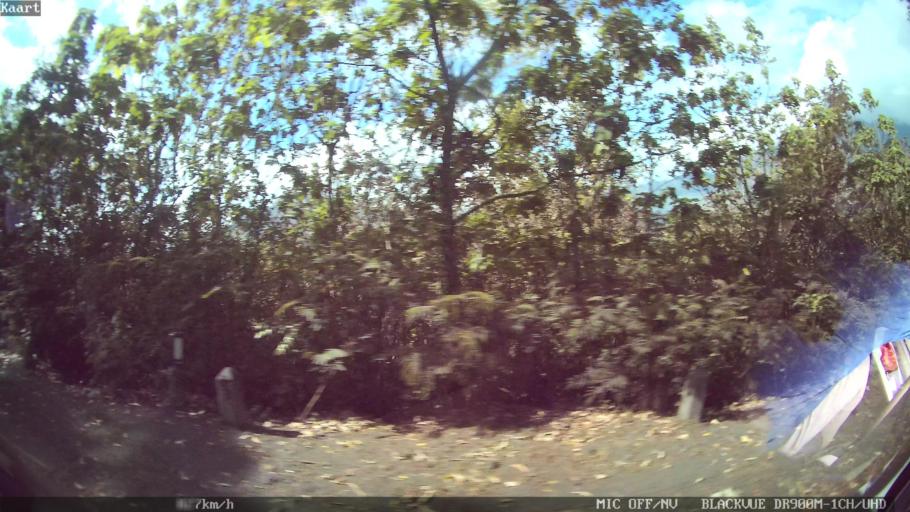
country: ID
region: Bali
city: Banjar Kedisan
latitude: -8.2799
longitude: 115.3705
